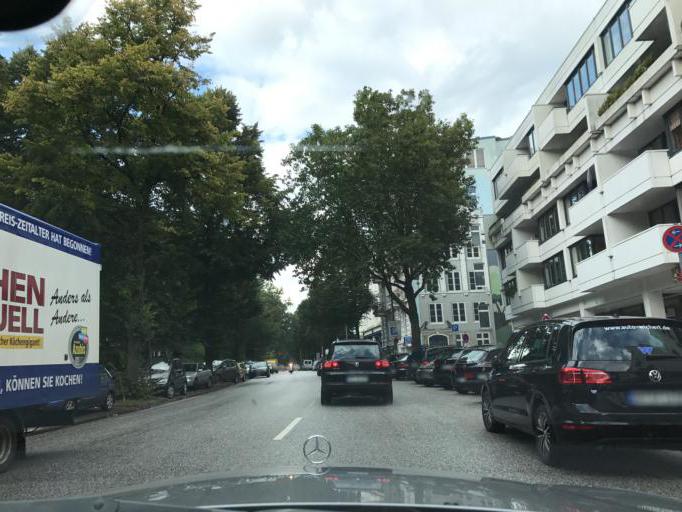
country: DE
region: Hamburg
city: Eimsbuettel
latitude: 53.5706
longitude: 9.9951
